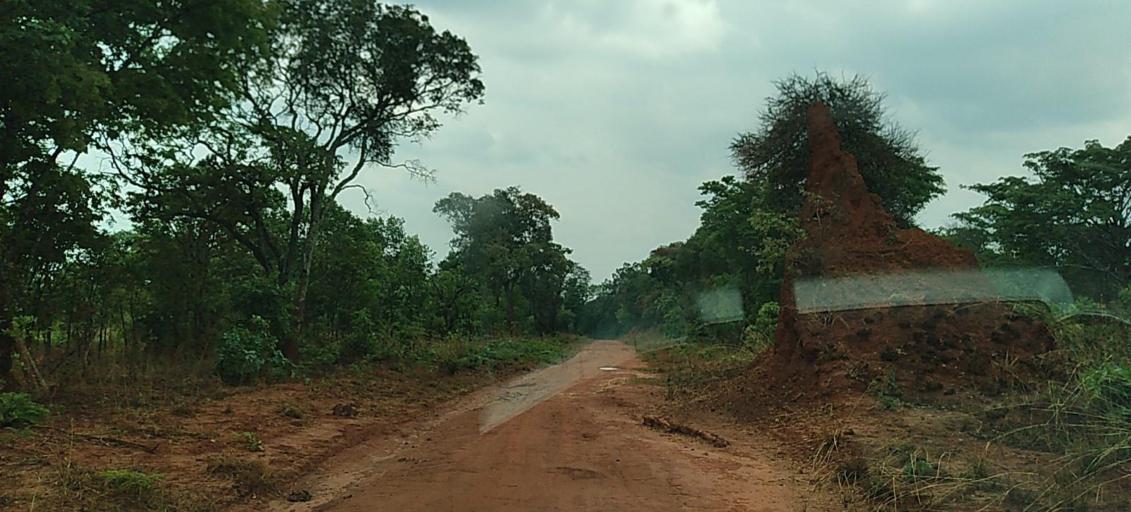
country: ZM
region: North-Western
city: Mwinilunga
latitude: -11.5433
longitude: 24.7794
